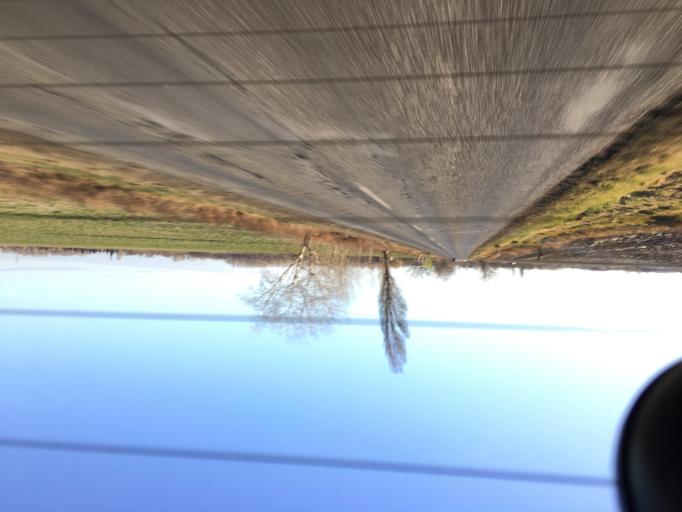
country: HU
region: Pest
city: Rackeve
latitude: 47.1709
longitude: 18.9704
